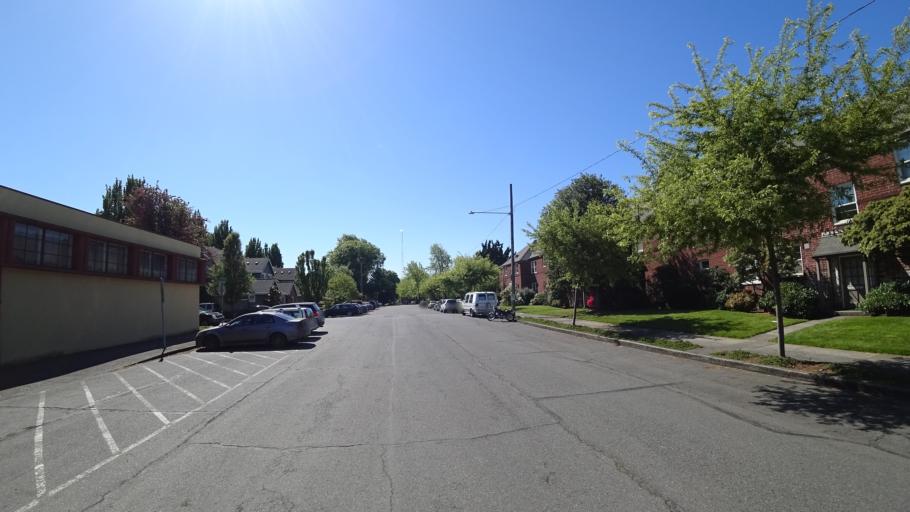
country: US
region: Oregon
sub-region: Multnomah County
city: Portland
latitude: 45.5266
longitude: -122.6482
